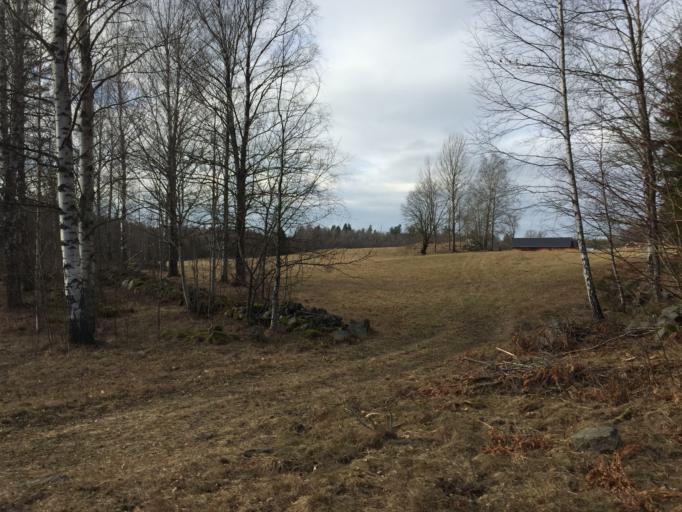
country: SE
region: Soedermanland
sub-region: Vingakers Kommun
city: Vingaker
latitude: 58.9942
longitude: 15.6712
